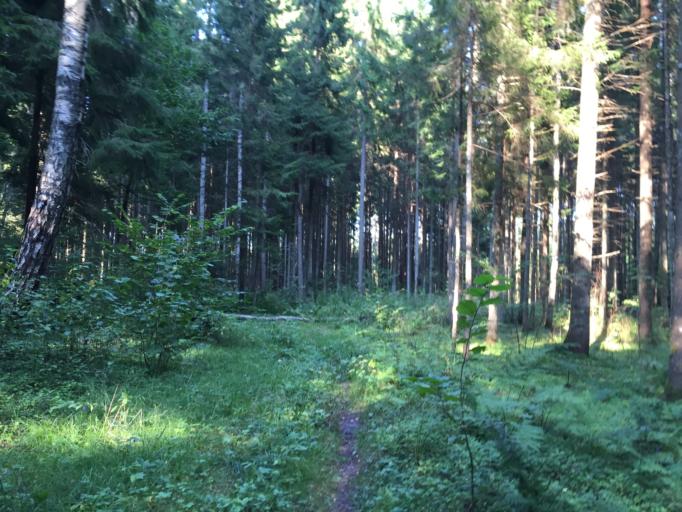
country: LV
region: Limbazu Rajons
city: Limbazi
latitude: 57.5658
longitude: 24.8002
